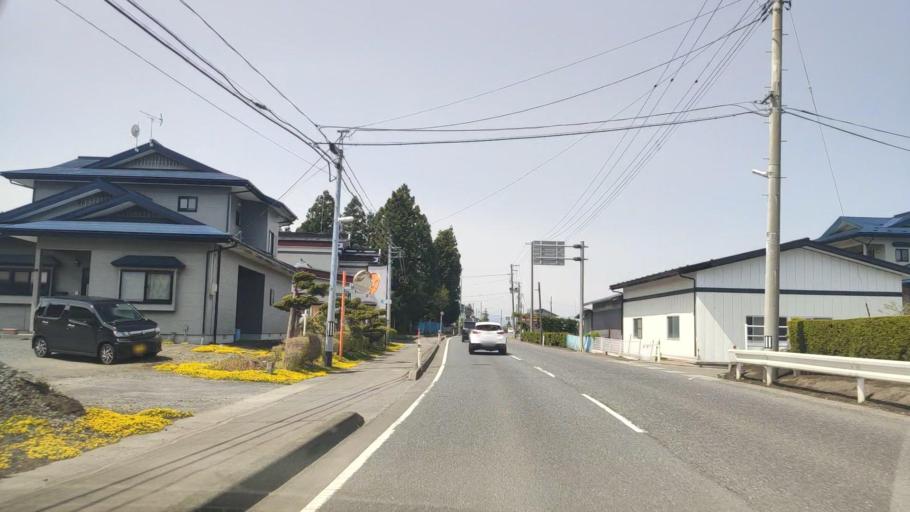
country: JP
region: Aomori
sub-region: Misawa Shi
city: Inuotose
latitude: 40.5914
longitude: 141.3483
